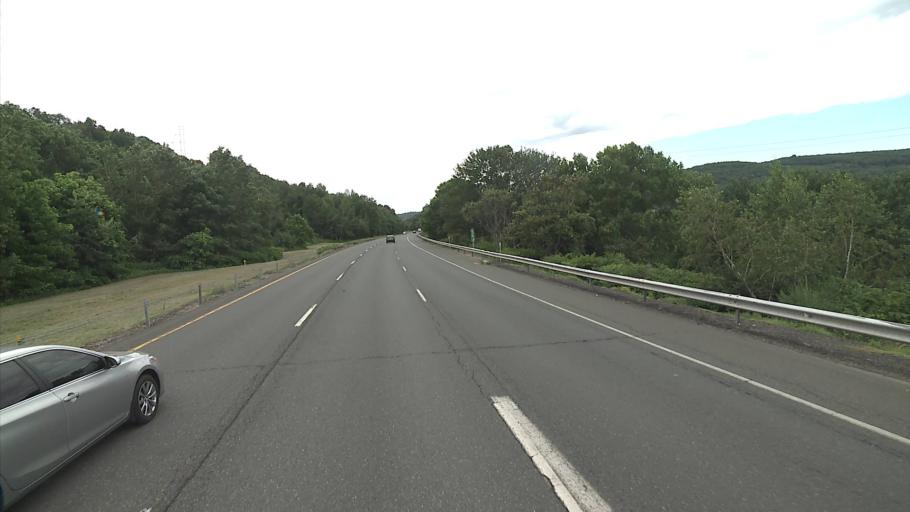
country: US
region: Connecticut
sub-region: Litchfield County
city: Thomaston
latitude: 41.6707
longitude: -73.0694
